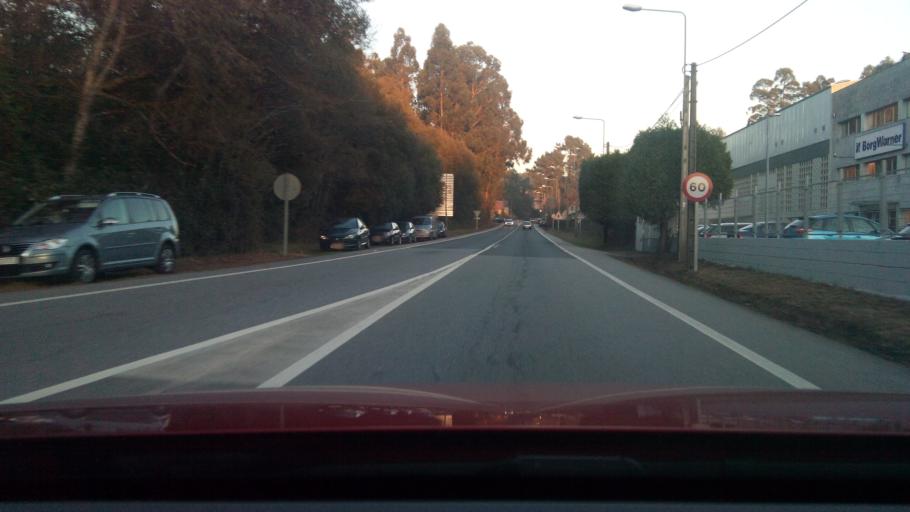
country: ES
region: Galicia
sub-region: Provincia de Pontevedra
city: Gondomar
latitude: 42.1572
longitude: -8.7155
